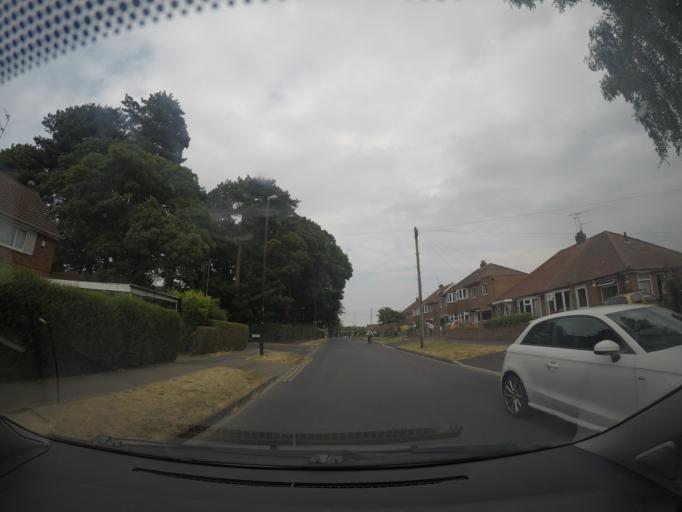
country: GB
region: England
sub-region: City of York
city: York
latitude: 53.9518
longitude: -1.1132
